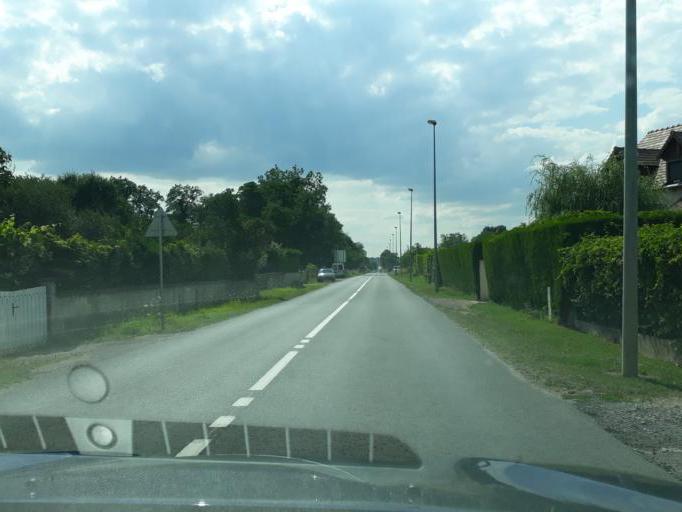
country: FR
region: Bourgogne
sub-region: Departement de la Nievre
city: Fourchambault
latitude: 47.0131
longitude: 3.0655
